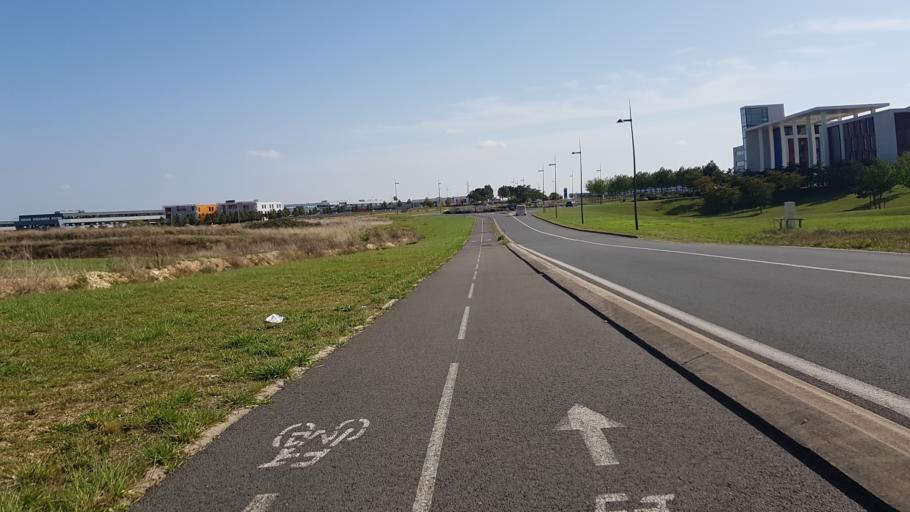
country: FR
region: Poitou-Charentes
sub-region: Departement de la Vienne
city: Chasseneuil-du-Poitou
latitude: 46.6563
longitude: 0.3582
